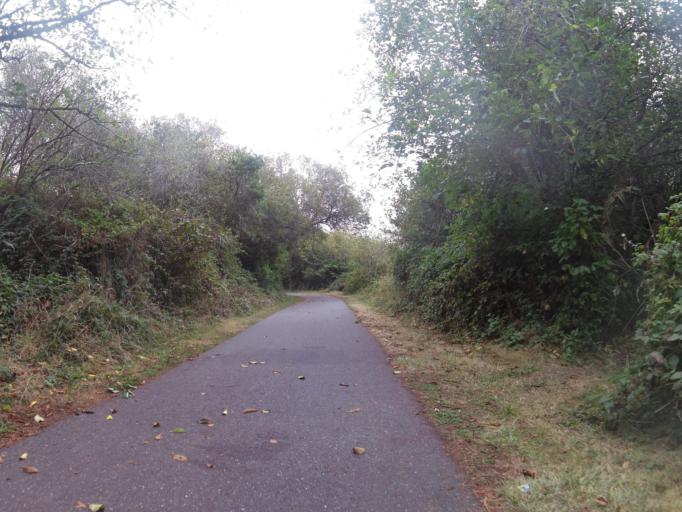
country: US
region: California
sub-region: Humboldt County
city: Bayview
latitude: 40.7652
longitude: -124.1965
